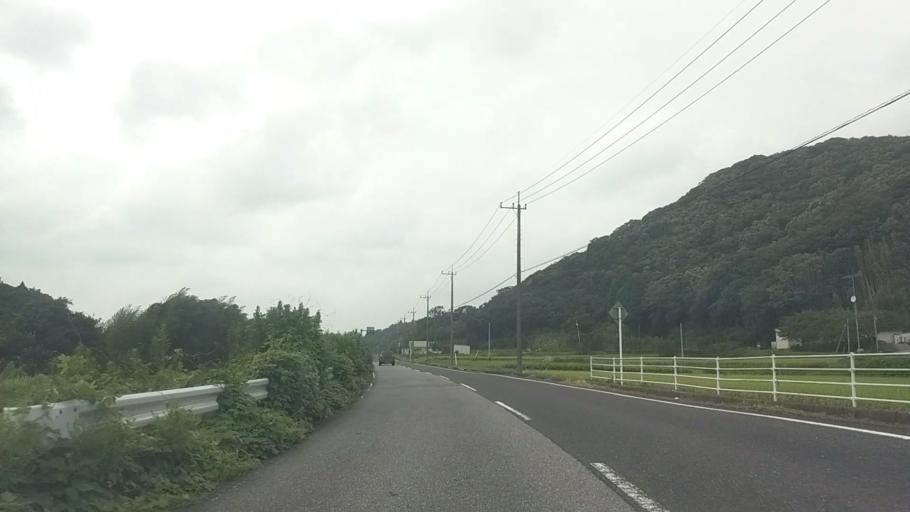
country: JP
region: Chiba
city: Kimitsu
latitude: 35.2628
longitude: 140.0044
